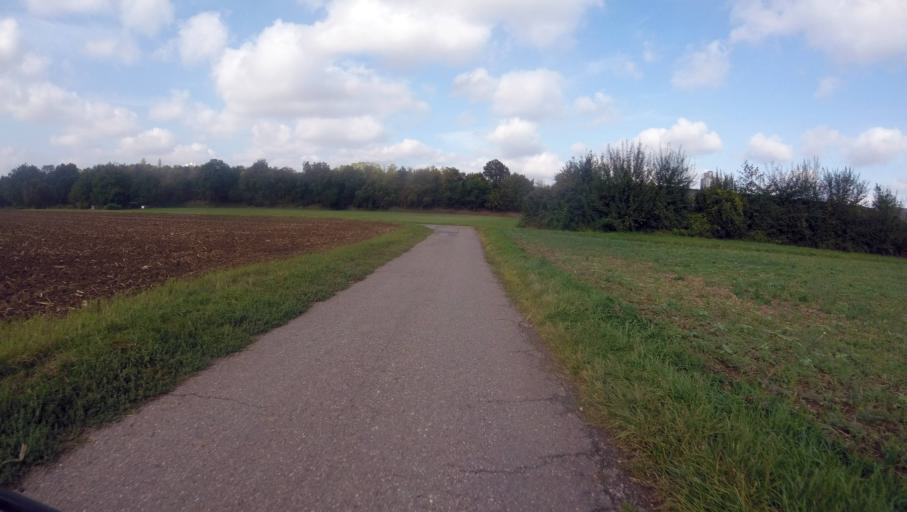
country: DE
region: Baden-Wuerttemberg
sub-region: Regierungsbezirk Stuttgart
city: Stuttgart Muehlhausen
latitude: 48.8708
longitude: 9.2696
